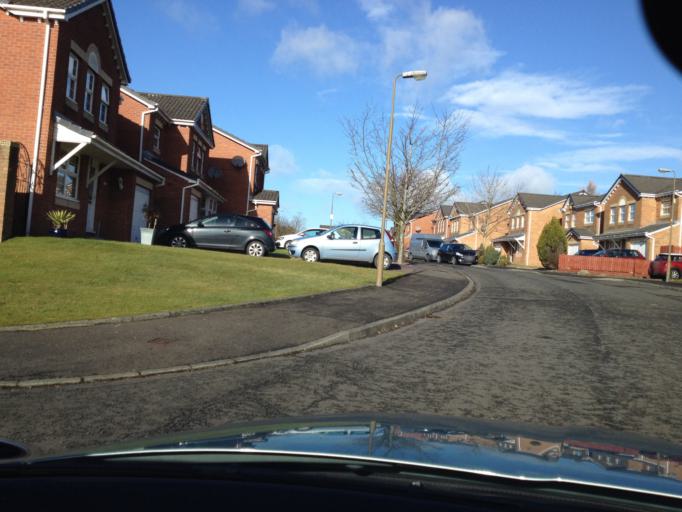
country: GB
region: Scotland
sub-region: West Lothian
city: Livingston
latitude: 55.8911
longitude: -3.5448
